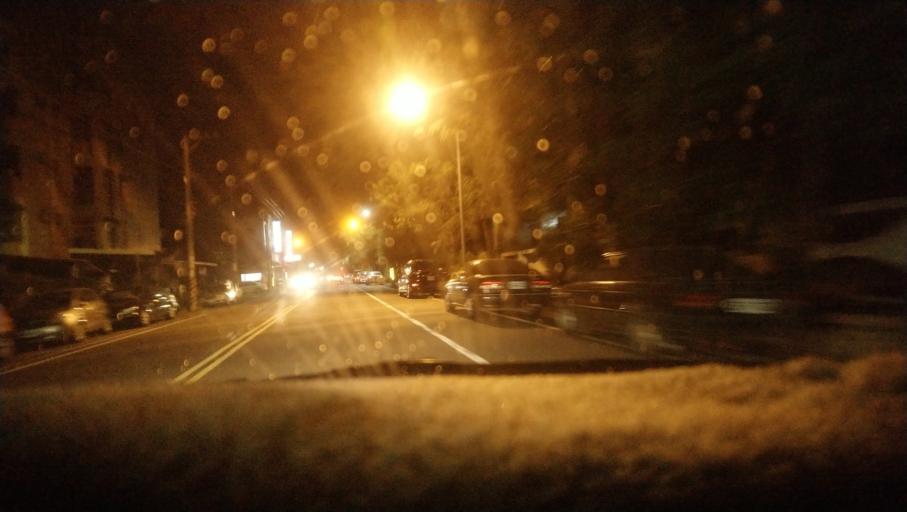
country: TW
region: Taiwan
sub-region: Yunlin
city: Douliu
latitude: 23.7103
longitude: 120.4412
